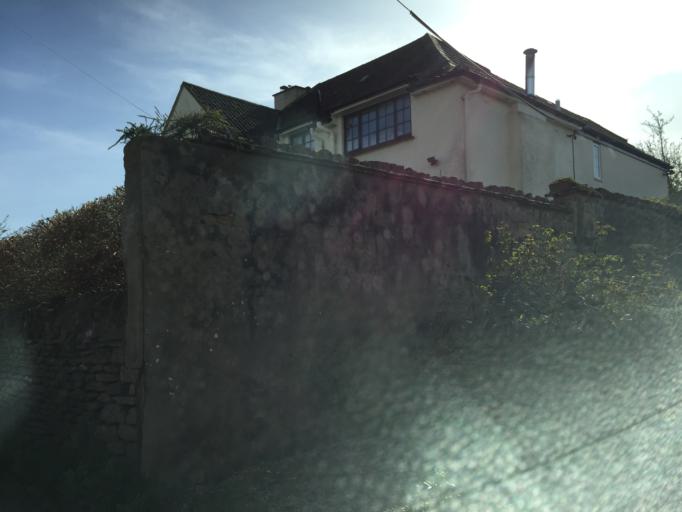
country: GB
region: England
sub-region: Wiltshire
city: Chippenham
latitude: 51.4961
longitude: -2.1404
